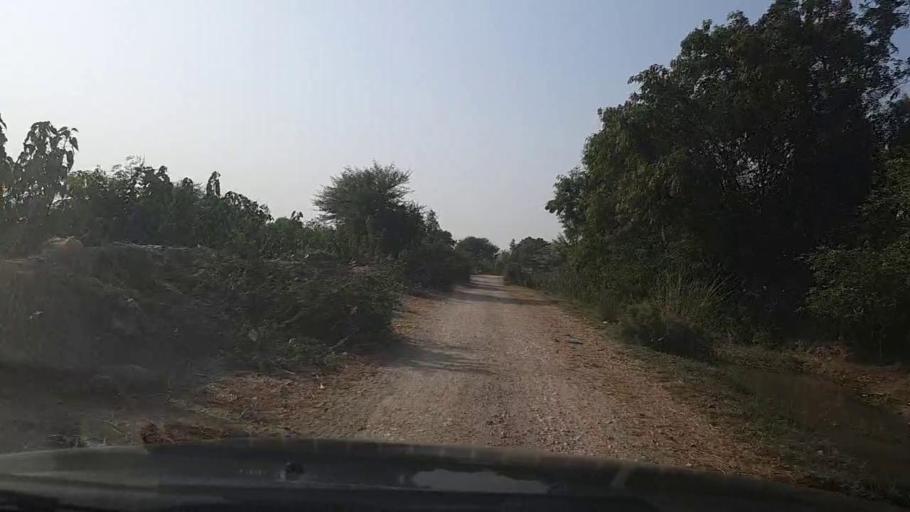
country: PK
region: Sindh
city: Mirpur Sakro
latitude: 24.6389
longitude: 67.7465
